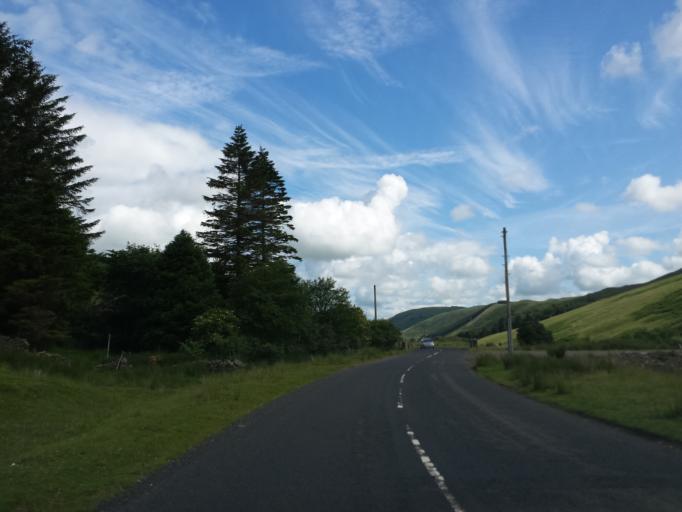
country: GB
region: Scotland
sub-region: The Scottish Borders
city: Peebles
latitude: 55.4496
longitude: -3.2222
